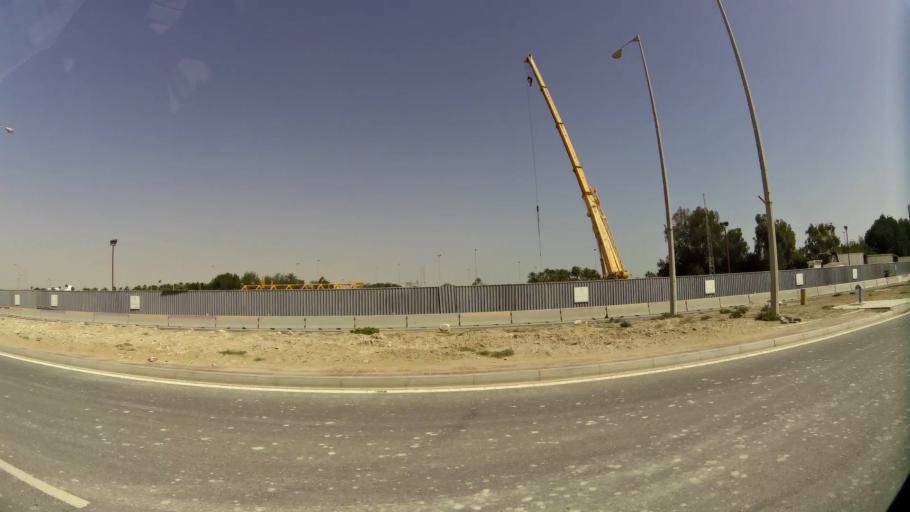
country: QA
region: Baladiyat ad Dawhah
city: Doha
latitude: 25.3775
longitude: 51.5067
